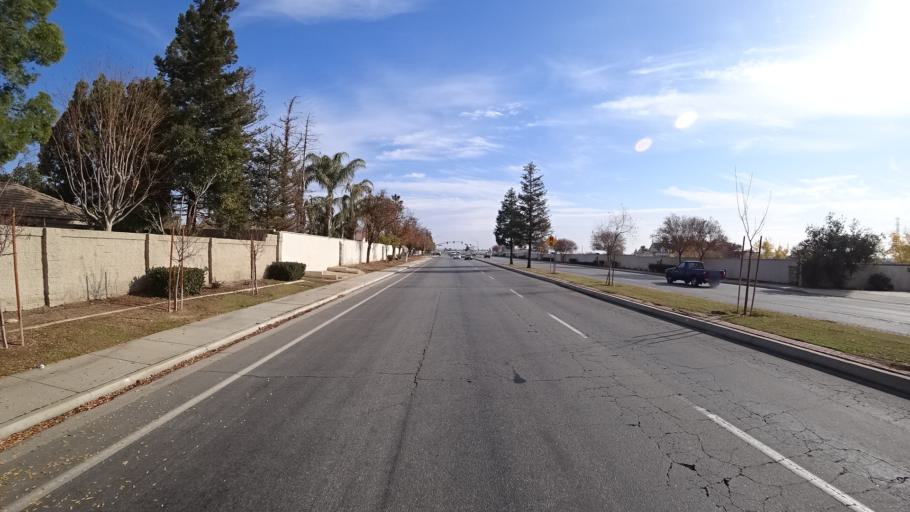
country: US
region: California
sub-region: Kern County
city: Greenacres
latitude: 35.4017
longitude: -119.0678
